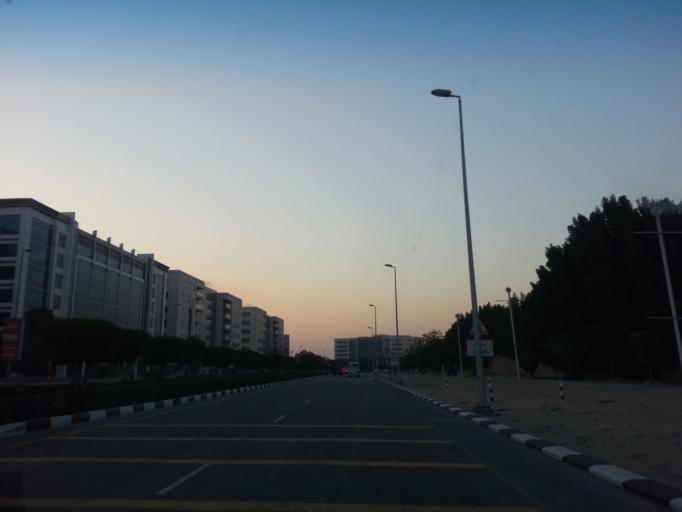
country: AE
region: Dubai
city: Dubai
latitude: 24.9985
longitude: 55.1735
